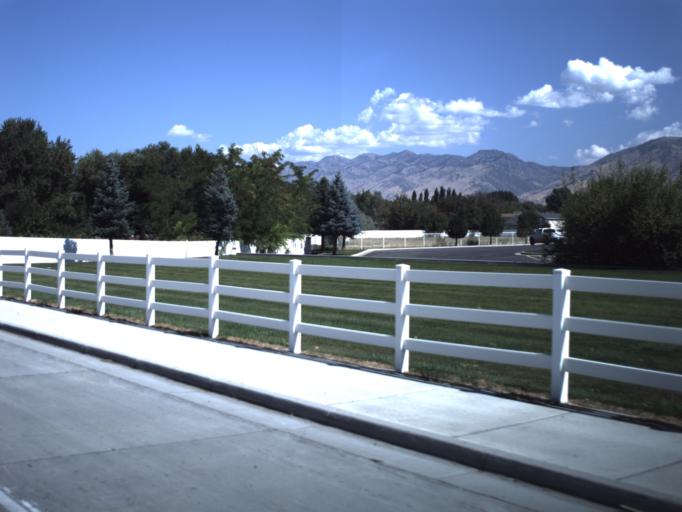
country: US
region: Utah
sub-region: Cache County
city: Logan
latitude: 41.7137
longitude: -111.8601
